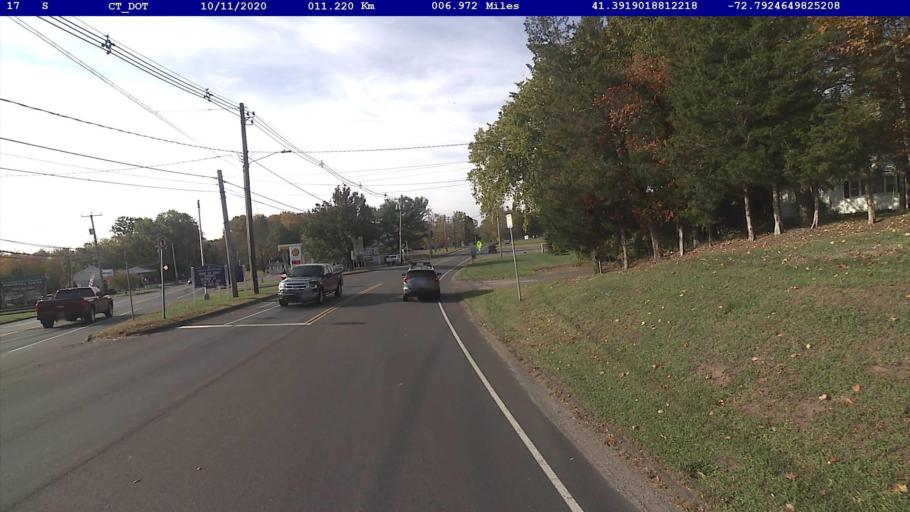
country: US
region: Connecticut
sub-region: New Haven County
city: Wallingford Center
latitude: 41.3919
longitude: -72.7925
